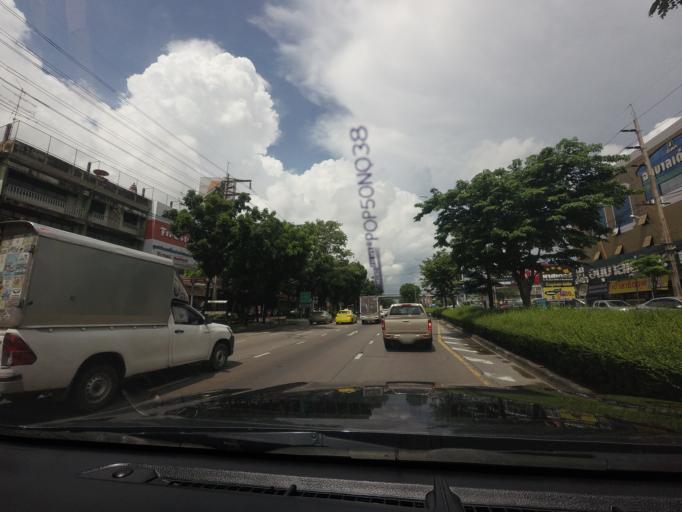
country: TH
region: Bangkok
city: Nong Khaem
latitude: 13.7083
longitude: 100.3792
